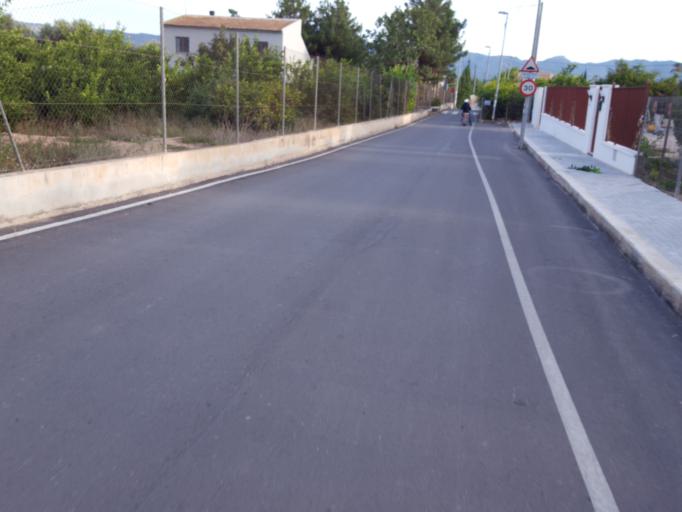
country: ES
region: Murcia
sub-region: Murcia
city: Murcia
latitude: 37.9933
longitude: -1.1743
